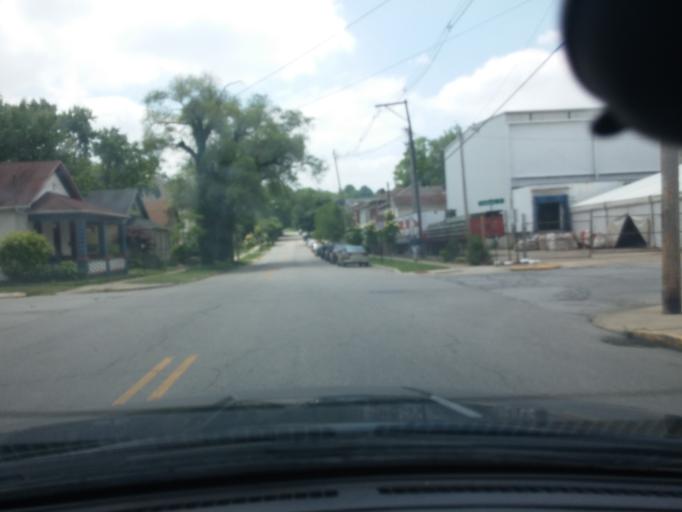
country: US
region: Indiana
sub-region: Tippecanoe County
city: Lafayette
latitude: 40.4166
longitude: -86.8906
